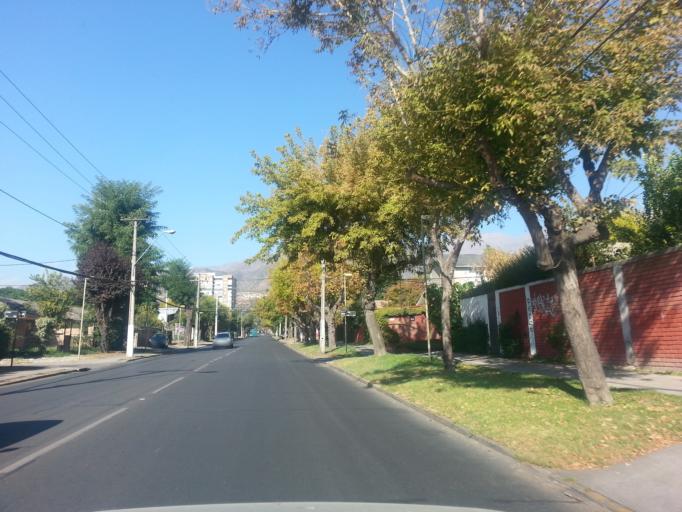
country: CL
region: Santiago Metropolitan
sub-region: Provincia de Santiago
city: Villa Presidente Frei, Nunoa, Santiago, Chile
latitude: -33.4245
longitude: -70.5445
